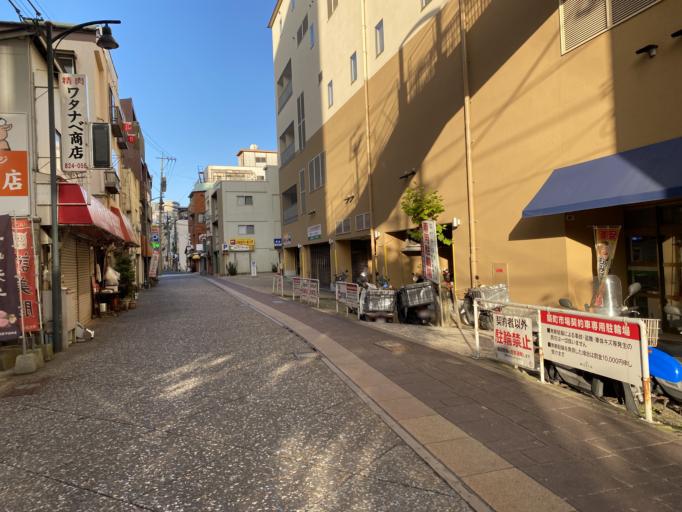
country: JP
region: Nagasaki
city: Nagasaki-shi
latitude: 32.7455
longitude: 129.8757
